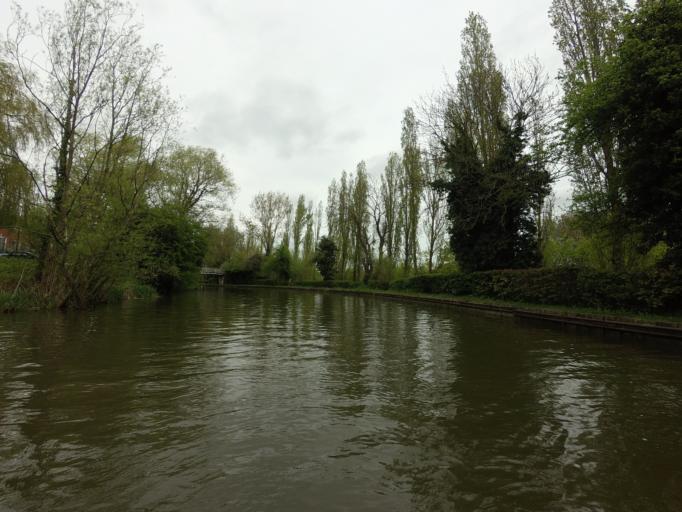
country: GB
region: England
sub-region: Milton Keynes
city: Milton Keynes
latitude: 52.0340
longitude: -0.7302
